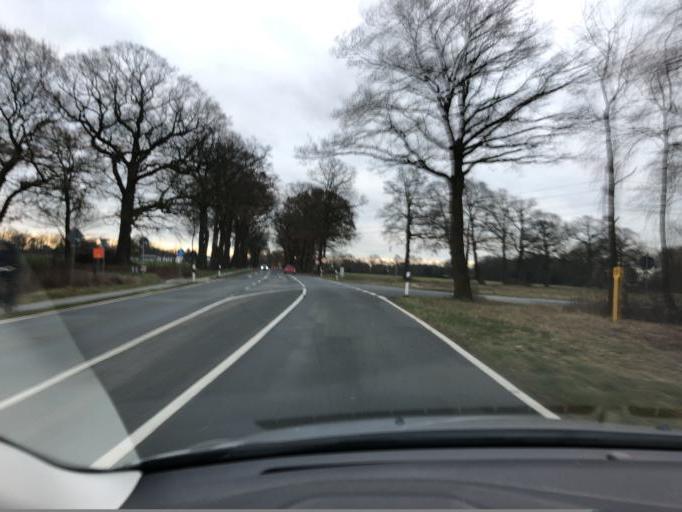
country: DE
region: Lower Saxony
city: Ganderkesee
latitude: 53.0678
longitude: 8.5679
